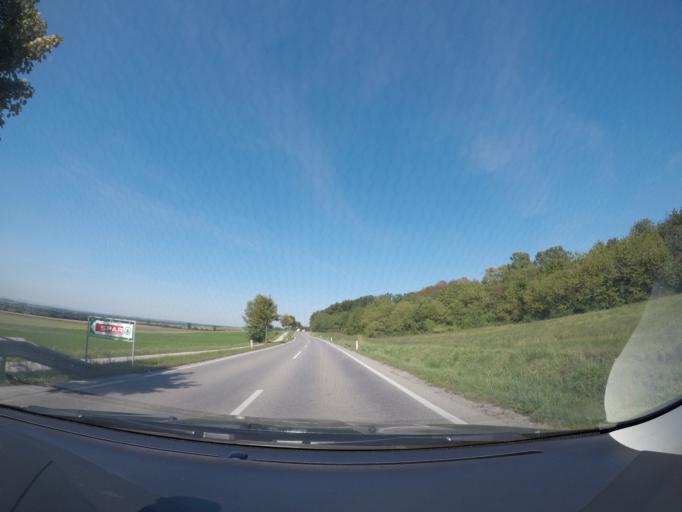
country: AT
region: Lower Austria
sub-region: Politischer Bezirk Bruck an der Leitha
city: Hof am Leithaberge
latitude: 47.9502
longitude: 16.5844
